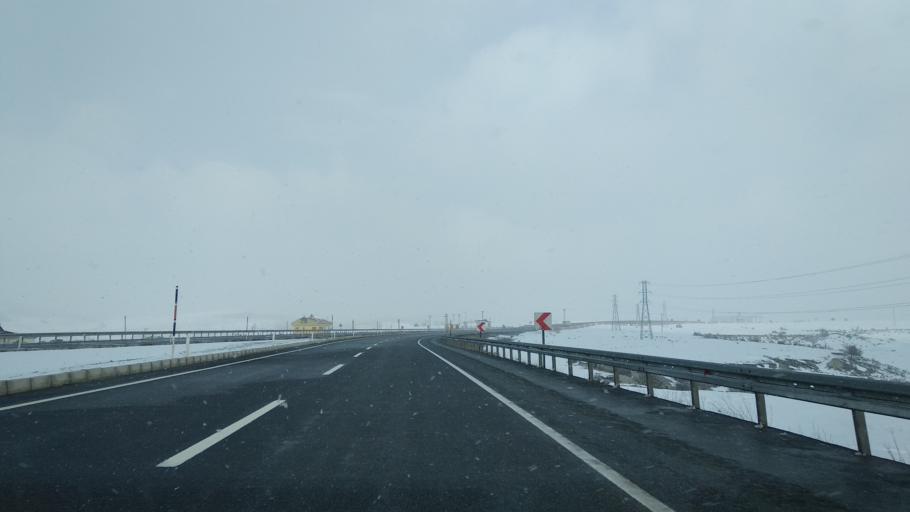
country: TR
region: Kayseri
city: Tomarza
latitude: 38.6292
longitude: 35.7609
